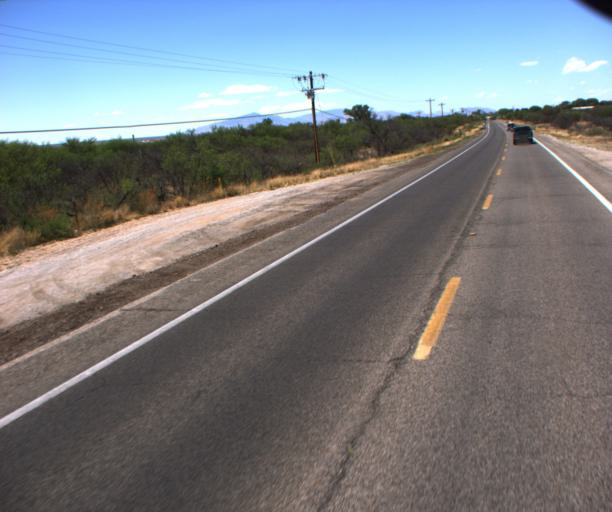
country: US
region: Arizona
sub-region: Cochise County
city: Saint David
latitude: 31.8599
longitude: -110.2035
